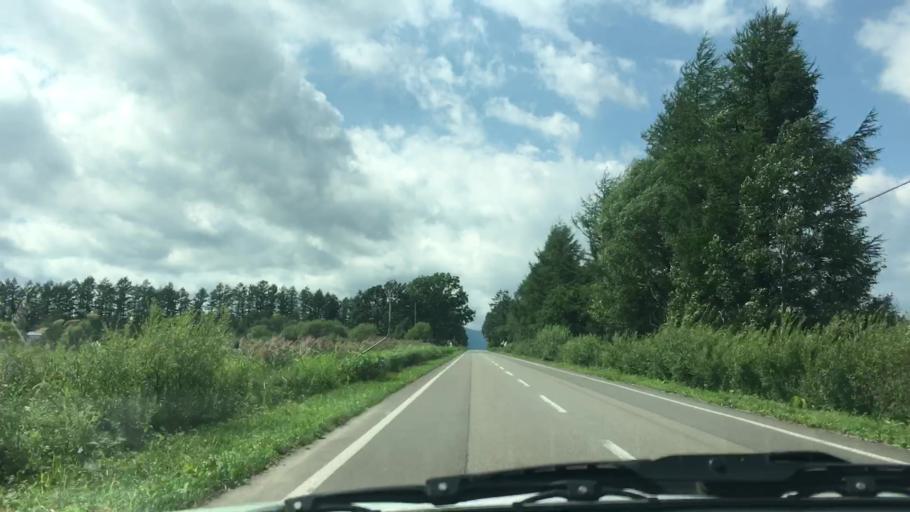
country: JP
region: Hokkaido
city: Otofuke
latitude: 43.2782
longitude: 143.3565
